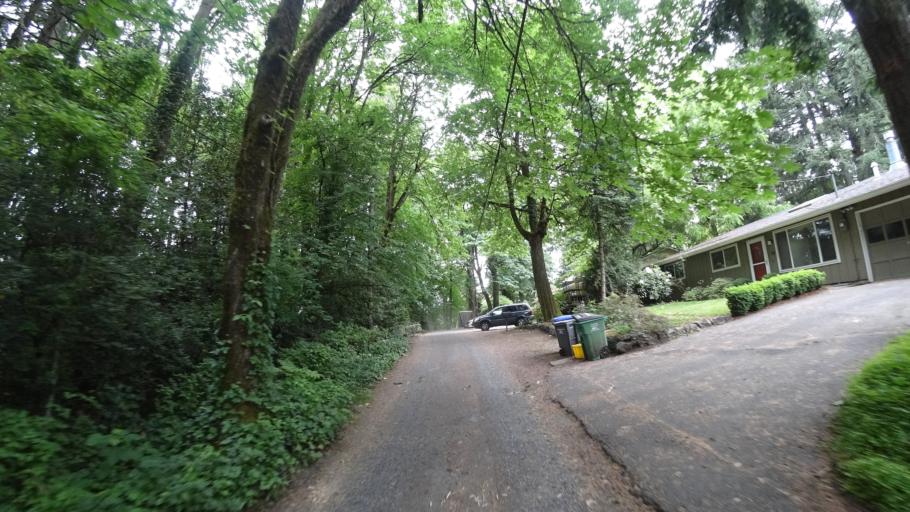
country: US
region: Oregon
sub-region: Clackamas County
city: Lake Oswego
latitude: 45.4549
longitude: -122.6785
